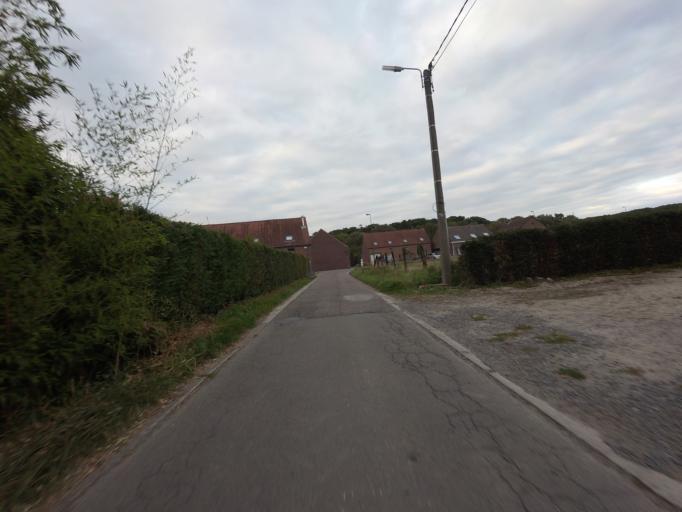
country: BE
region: Flanders
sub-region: Provincie Vlaams-Brabant
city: Boortmeerbeek
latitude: 50.9567
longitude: 4.5706
